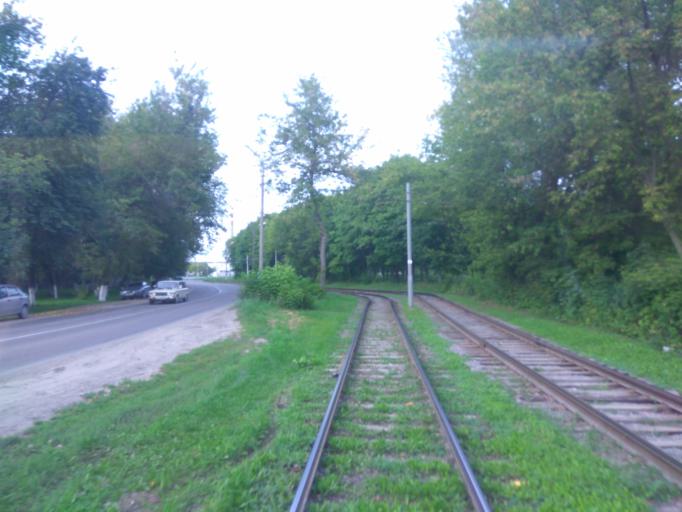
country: RU
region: Moskovskaya
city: Kolomna
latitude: 55.0779
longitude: 38.8164
